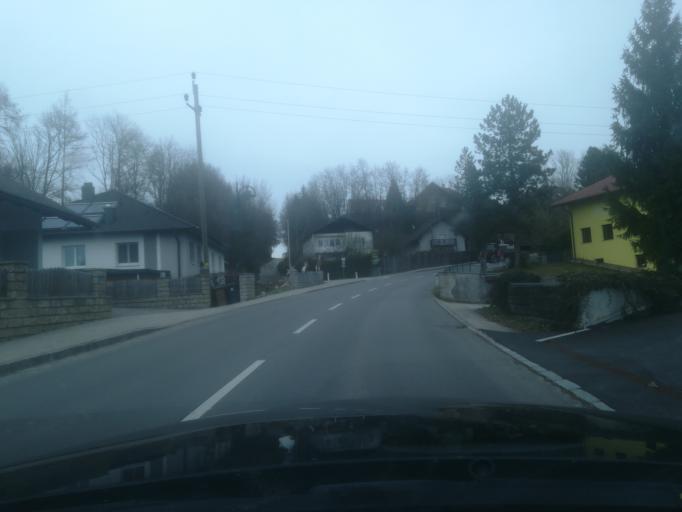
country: AT
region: Upper Austria
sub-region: Wels-Land
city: Gunskirchen
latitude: 48.0899
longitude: 13.9522
